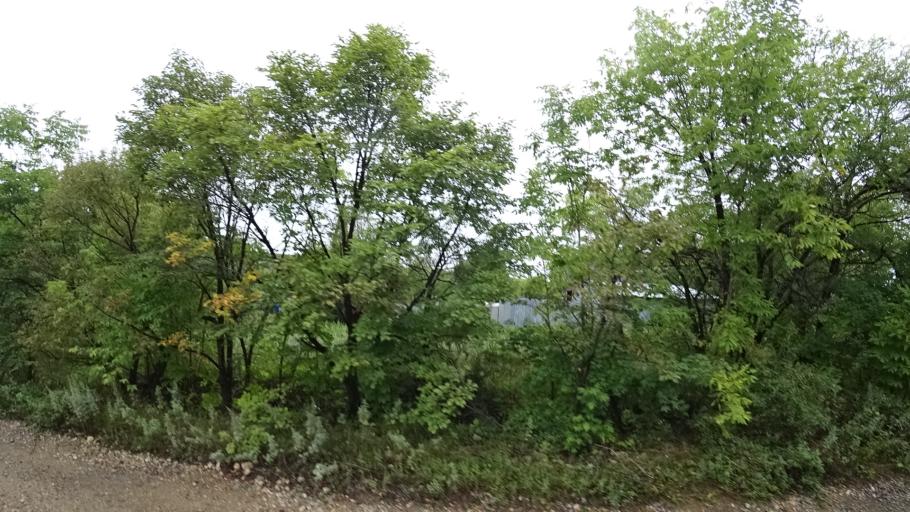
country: RU
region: Primorskiy
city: Monastyrishche
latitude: 44.2755
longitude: 132.4065
